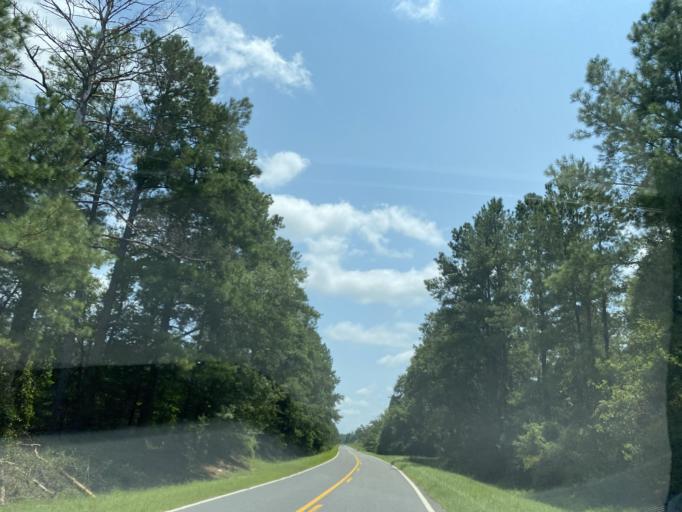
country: US
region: Georgia
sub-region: Telfair County
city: Lumber City
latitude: 31.9573
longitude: -82.6983
